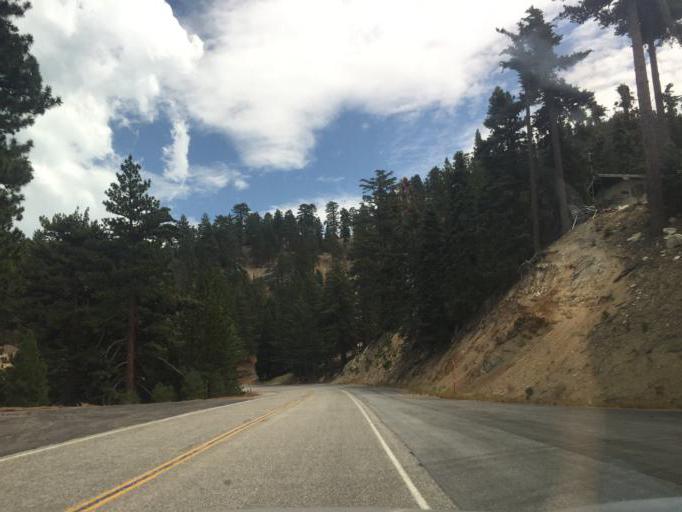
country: US
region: California
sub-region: Los Angeles County
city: Littlerock
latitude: 34.3522
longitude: -117.8989
